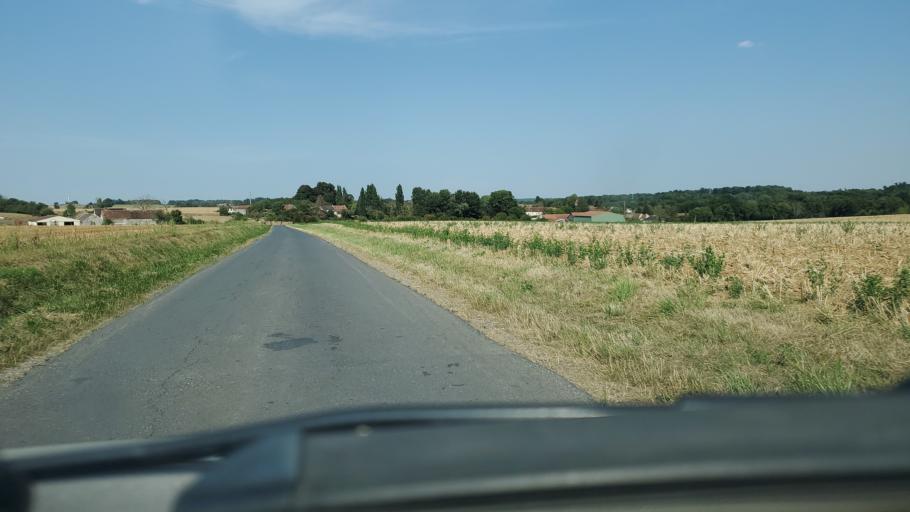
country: FR
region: Ile-de-France
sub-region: Departement de Seine-et-Marne
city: Chailly-en-Brie
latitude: 48.7718
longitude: 3.1560
